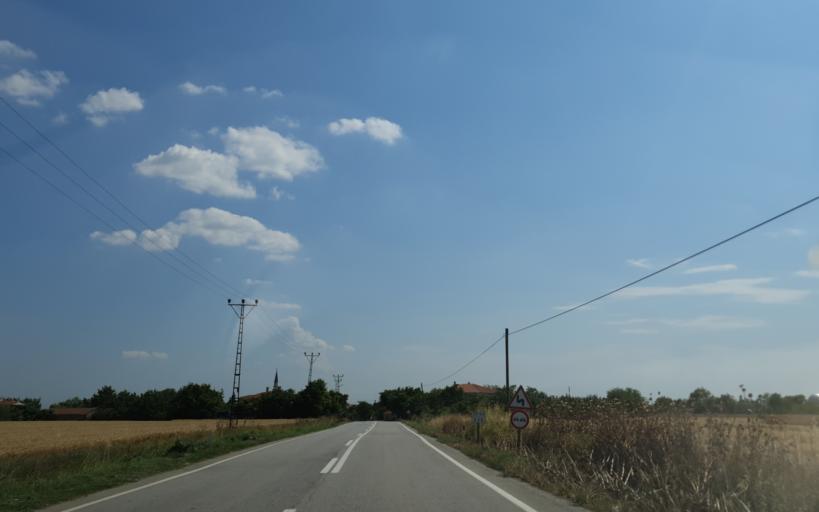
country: TR
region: Kirklareli
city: Buyukkaristiran
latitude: 41.3379
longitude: 27.5445
